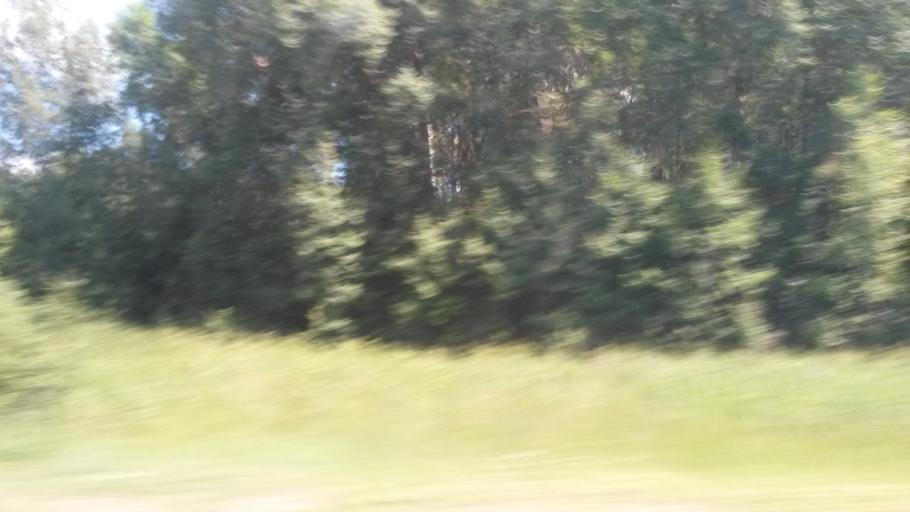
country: RU
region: Ivanovo
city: Rodniki
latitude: 57.1101
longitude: 41.7817
